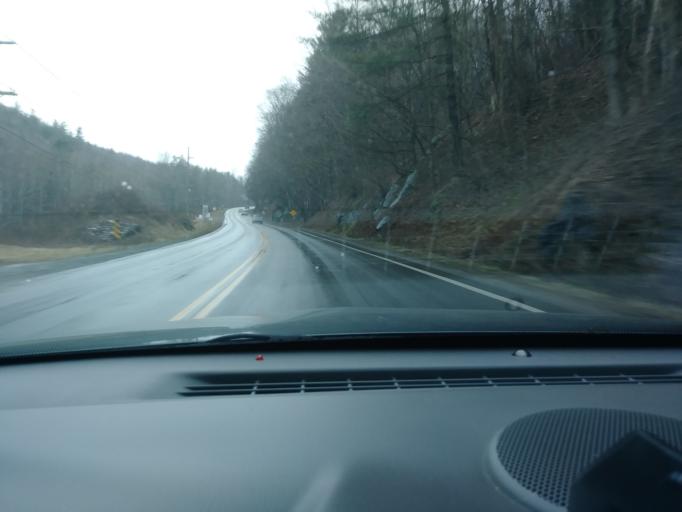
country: US
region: North Carolina
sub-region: Watauga County
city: Foscoe
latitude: 36.1936
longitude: -81.7456
